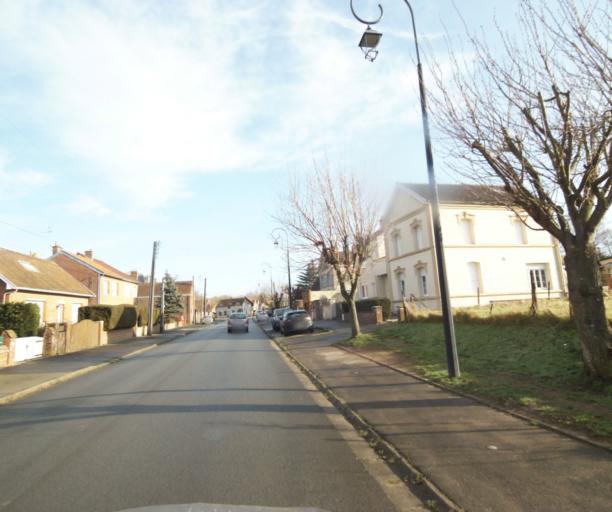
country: FR
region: Nord-Pas-de-Calais
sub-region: Departement du Nord
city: Maing
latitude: 50.3108
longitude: 3.4899
